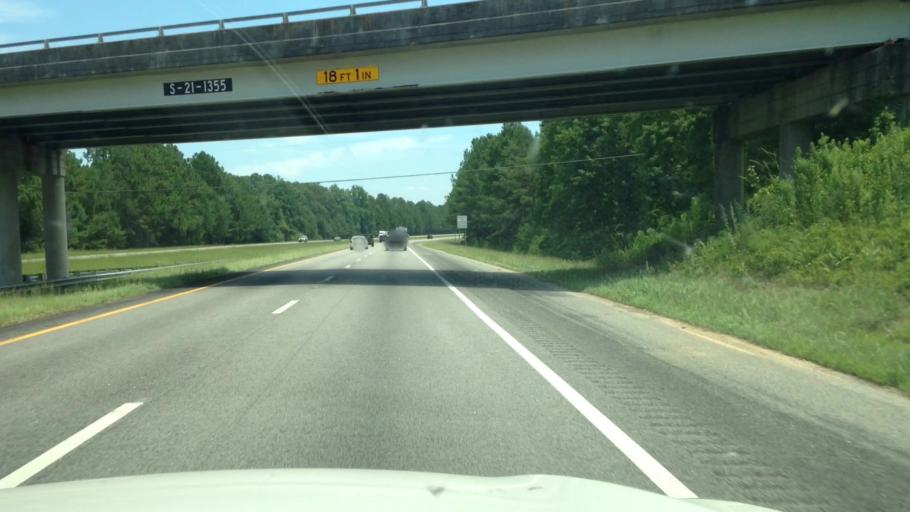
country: US
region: South Carolina
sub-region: Florence County
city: Timmonsville
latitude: 34.2040
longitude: -79.8798
